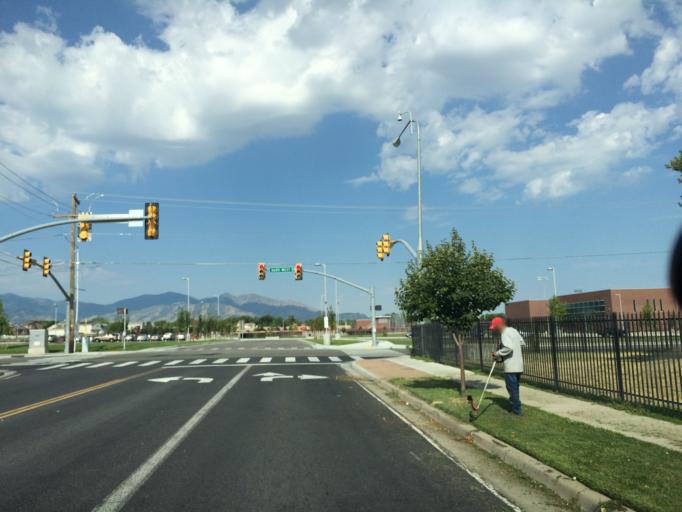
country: US
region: Utah
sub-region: Salt Lake County
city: West Valley City
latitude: 40.6929
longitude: -111.9765
